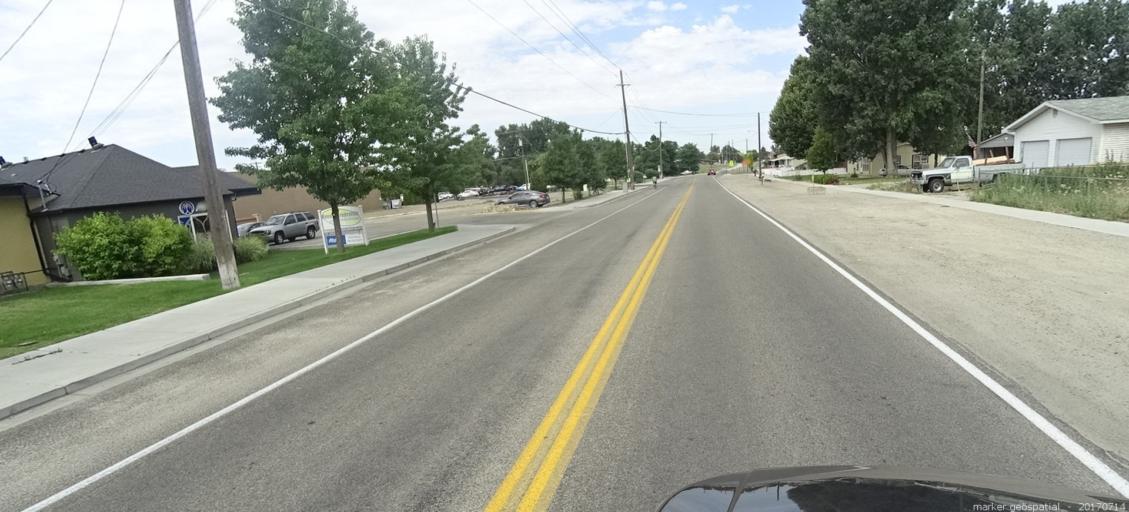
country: US
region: Idaho
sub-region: Ada County
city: Kuna
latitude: 43.4918
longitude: -116.4212
